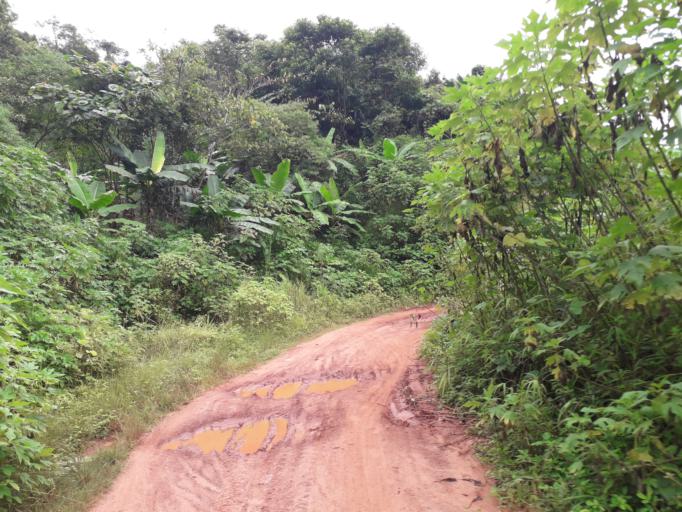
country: CN
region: Yunnan
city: Menglie
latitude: 22.2403
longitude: 101.6166
